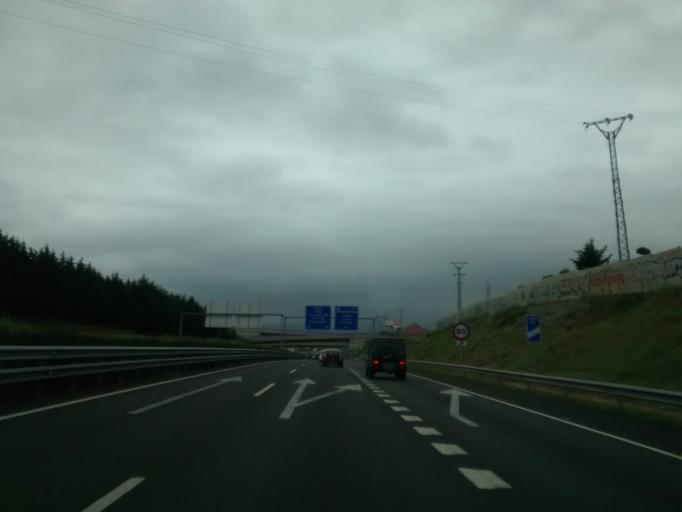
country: ES
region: Cantabria
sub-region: Provincia de Cantabria
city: Santa Cruz de Bezana
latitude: 43.4376
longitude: -3.8807
